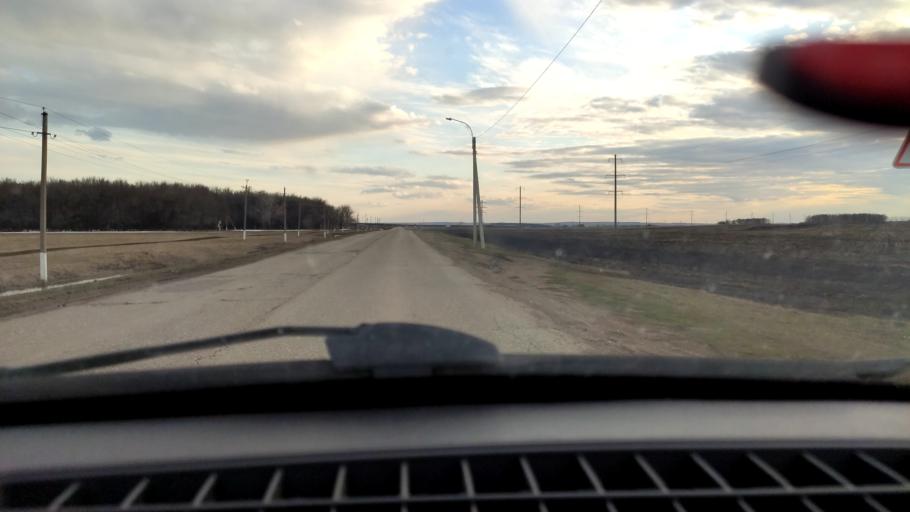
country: RU
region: Bashkortostan
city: Tolbazy
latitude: 53.9995
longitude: 55.8561
